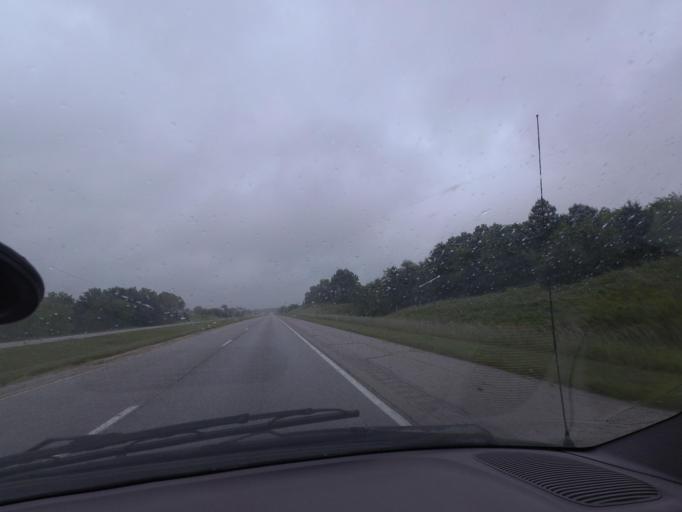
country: US
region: Illinois
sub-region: Pike County
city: Pittsfield
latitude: 39.6821
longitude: -90.8744
